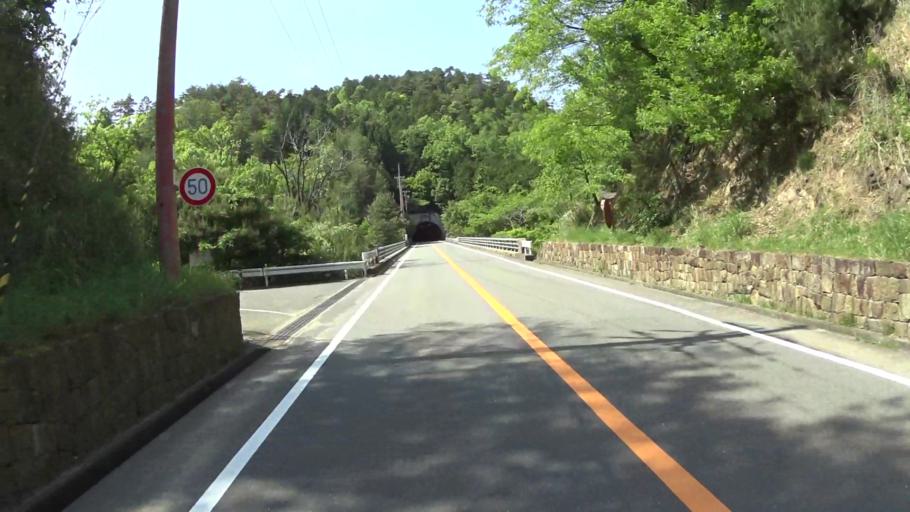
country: JP
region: Kyoto
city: Kameoka
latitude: 35.1331
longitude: 135.5359
